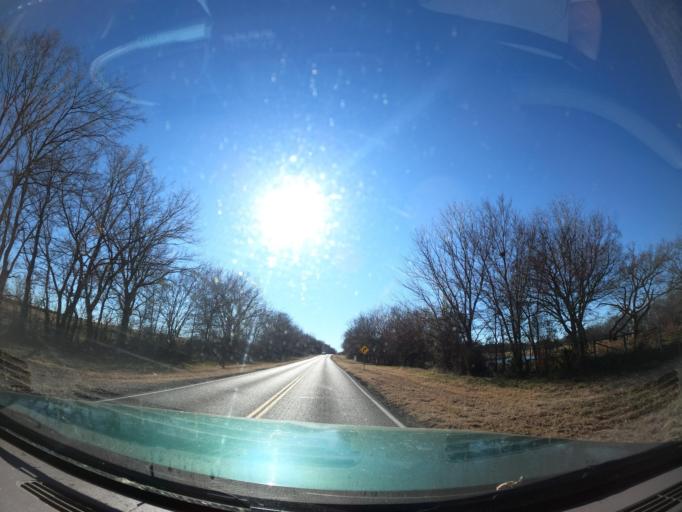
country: US
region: Oklahoma
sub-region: Muskogee County
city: Haskell
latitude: 35.6639
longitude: -95.6451
